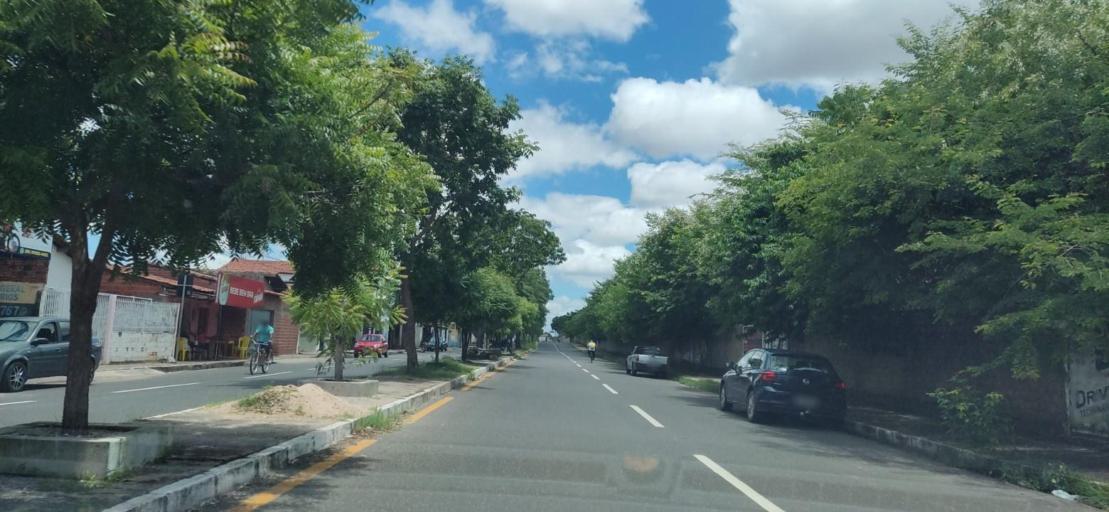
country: BR
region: Piaui
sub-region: Teresina
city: Teresina
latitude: -5.0647
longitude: -42.7549
